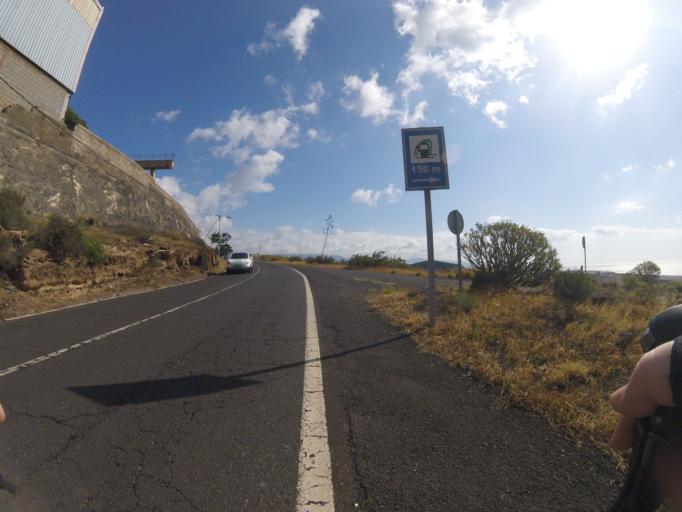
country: ES
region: Canary Islands
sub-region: Provincia de Santa Cruz de Tenerife
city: La Laguna
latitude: 28.4174
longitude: -16.3208
